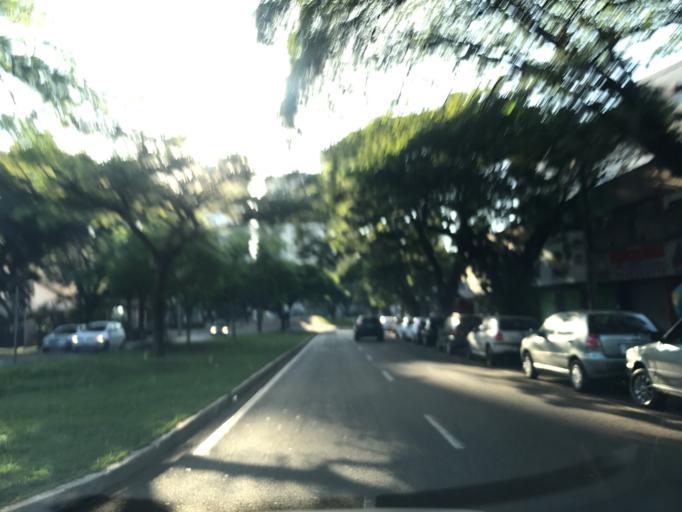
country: BR
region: Parana
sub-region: Maringa
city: Maringa
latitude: -23.4261
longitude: -51.9499
